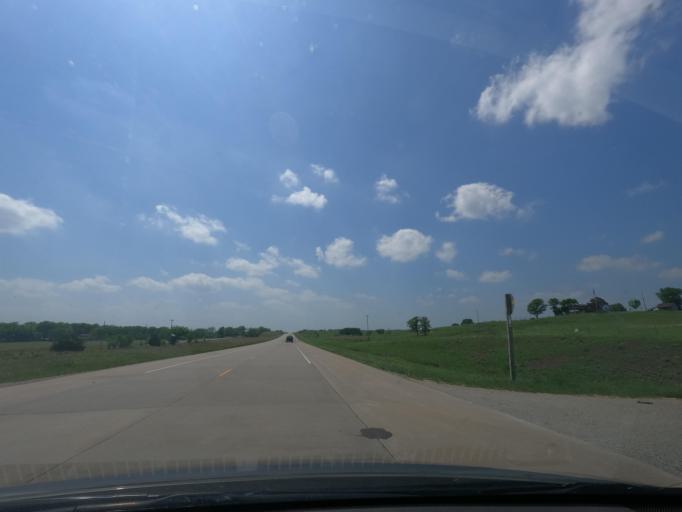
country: US
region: Kansas
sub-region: Elk County
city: Howard
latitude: 37.6275
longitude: -96.0790
